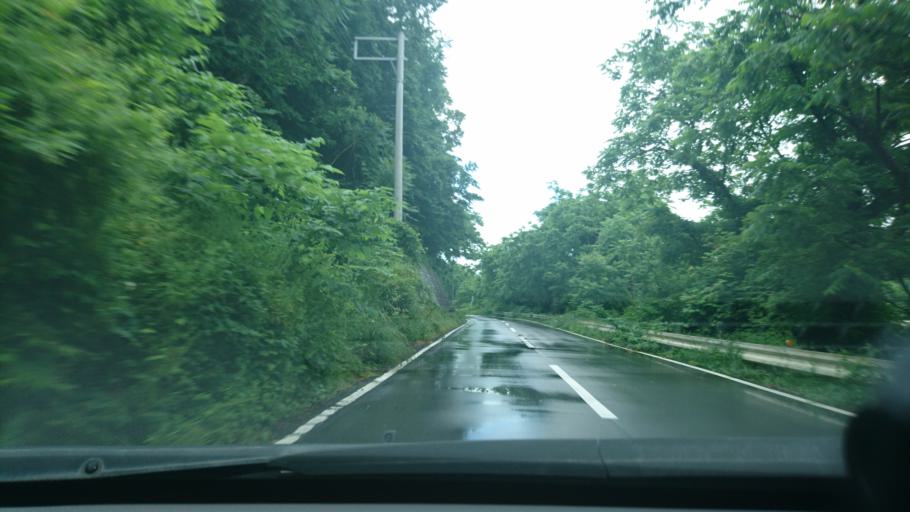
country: JP
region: Miyagi
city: Wakuya
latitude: 38.6662
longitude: 141.2838
